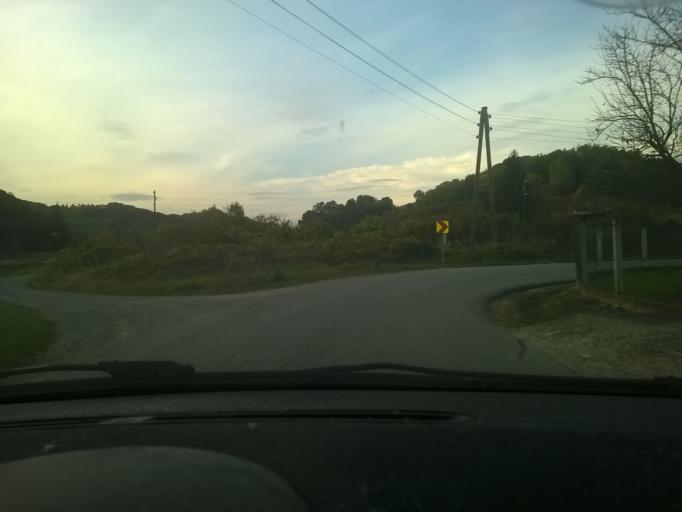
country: HR
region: Krapinsko-Zagorska
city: Zabok
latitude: 46.0842
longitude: 15.8911
